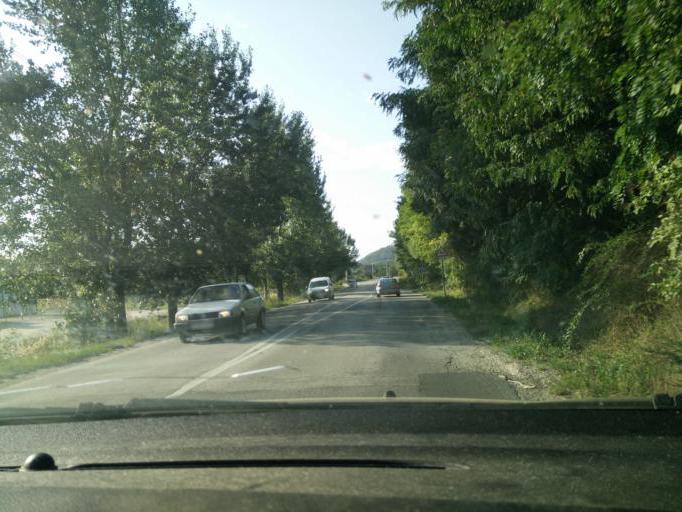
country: HU
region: Pest
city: Piliscsaba
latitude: 47.6438
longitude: 18.8089
